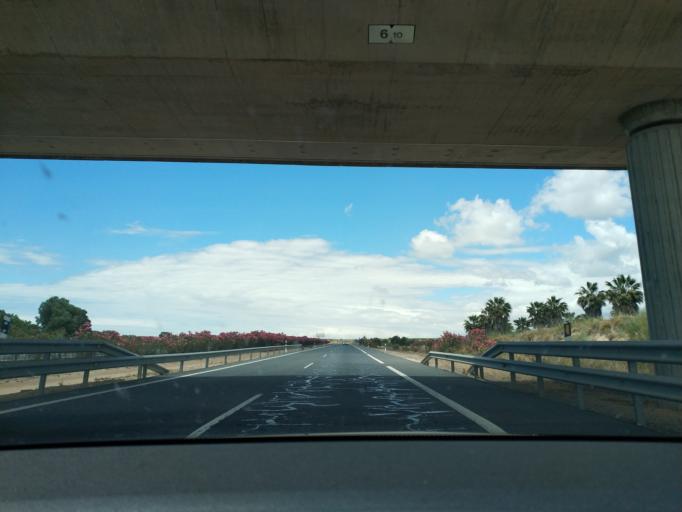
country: ES
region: Andalusia
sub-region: Provincia de Huelva
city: Aljaraque
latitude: 37.3357
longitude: -7.0229
